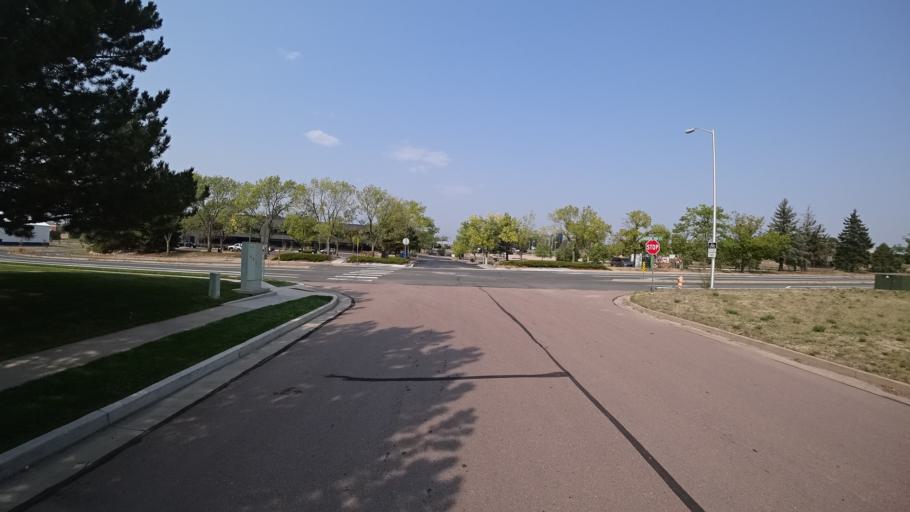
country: US
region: Colorado
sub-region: El Paso County
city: Stratmoor
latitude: 38.8122
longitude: -104.7528
